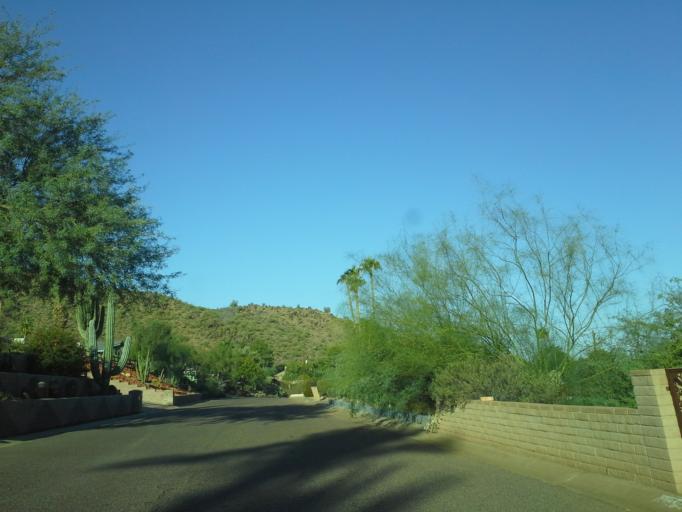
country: US
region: Arizona
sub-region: Maricopa County
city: Glendale
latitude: 33.6015
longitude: -112.0927
